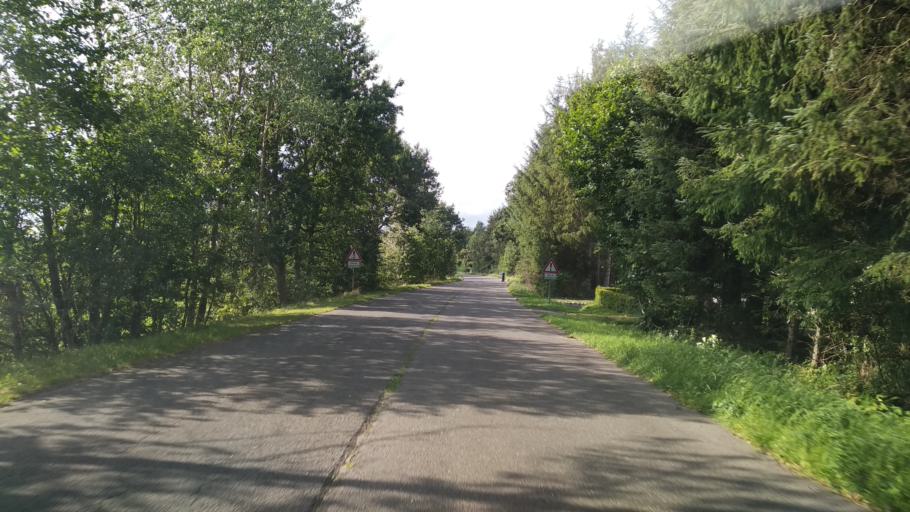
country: DE
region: Schleswig-Holstein
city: Neuberend
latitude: 54.5510
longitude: 9.5390
